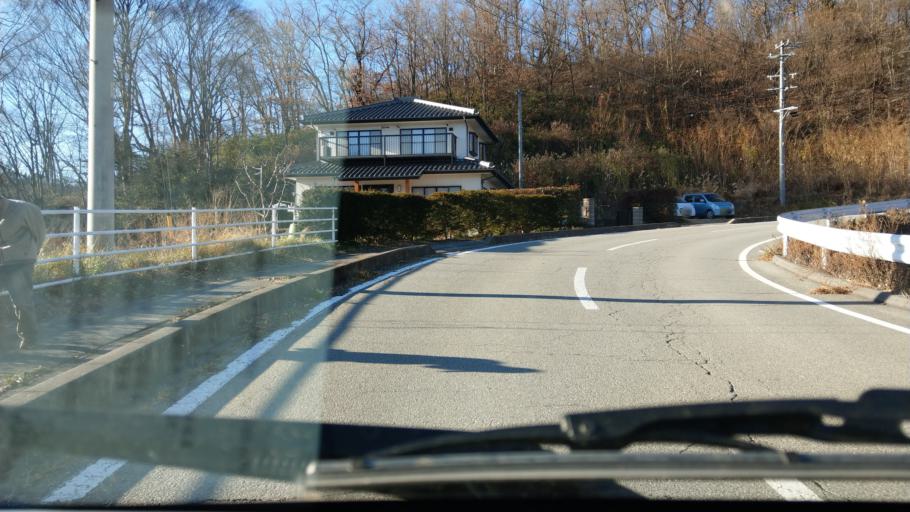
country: JP
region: Nagano
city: Komoro
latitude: 36.3205
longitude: 138.4212
